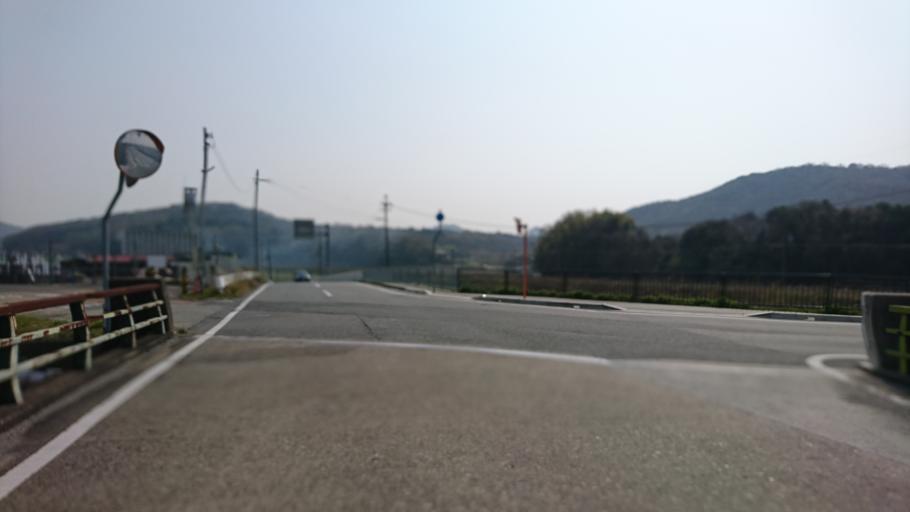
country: JP
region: Hyogo
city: Ono
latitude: 34.8513
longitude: 134.9101
